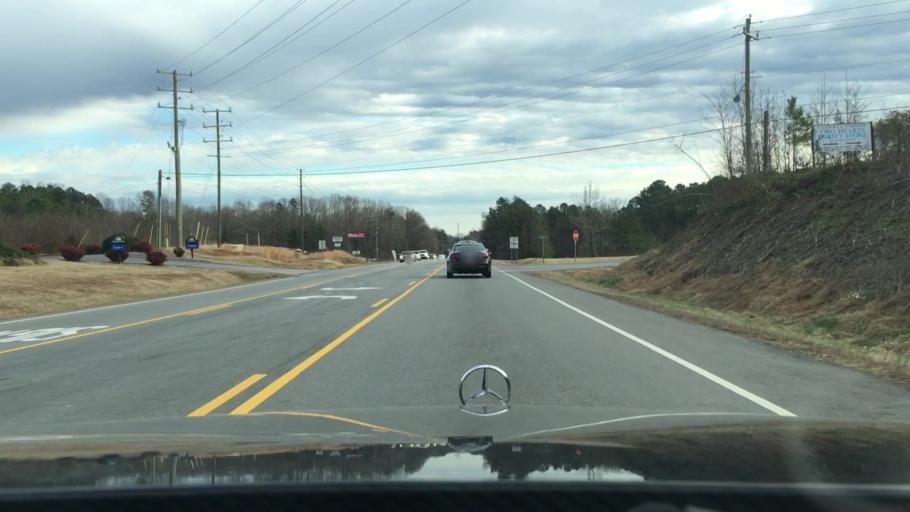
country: US
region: North Carolina
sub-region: Caswell County
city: Yanceyville
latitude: 36.4158
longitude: -79.3477
